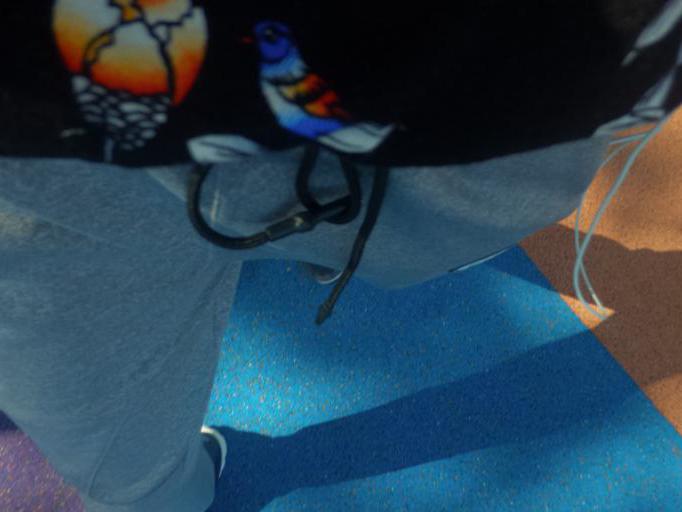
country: TW
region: Taipei
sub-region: Taipei
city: Banqiao
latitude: 25.0026
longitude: 121.4782
